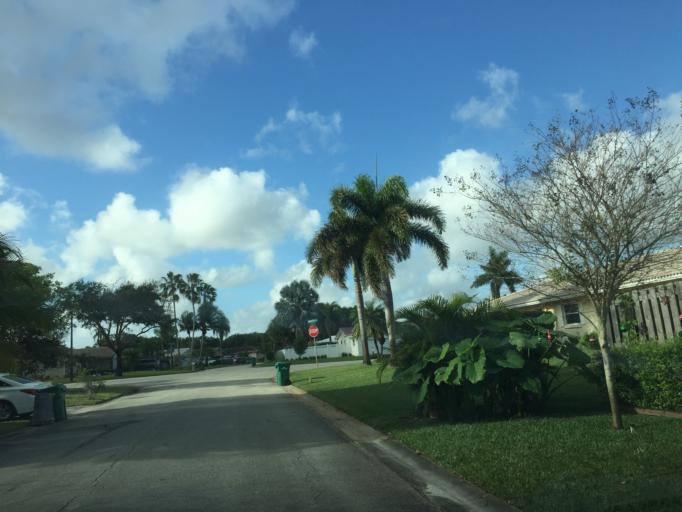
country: US
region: Florida
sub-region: Broward County
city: North Lauderdale
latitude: 26.2456
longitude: -80.2384
